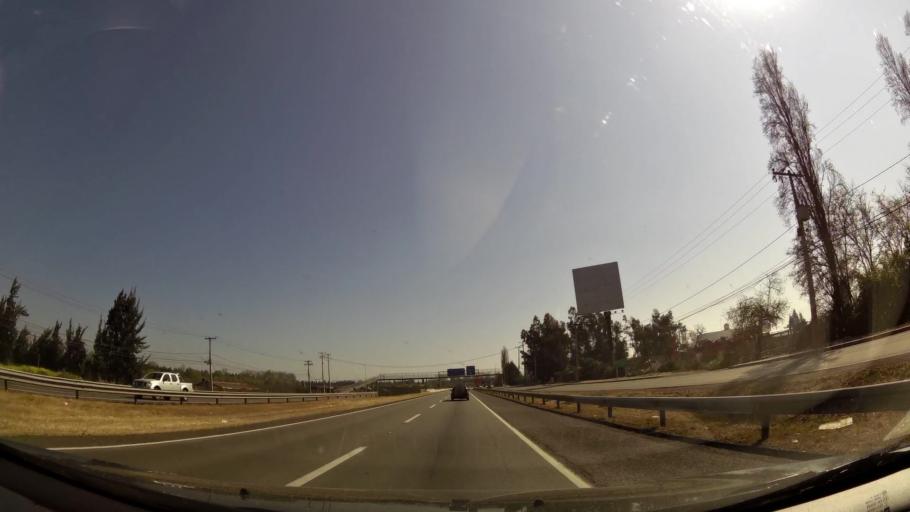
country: CL
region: Santiago Metropolitan
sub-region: Provincia de Chacabuco
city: Chicureo Abajo
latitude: -33.2957
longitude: -70.7012
